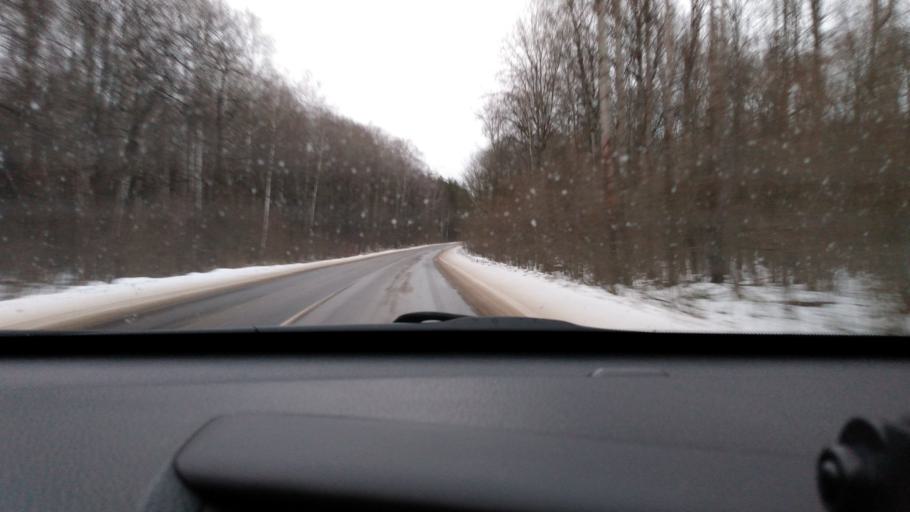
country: RU
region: Moskovskaya
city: Bronnitsy
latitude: 55.2930
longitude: 38.2298
